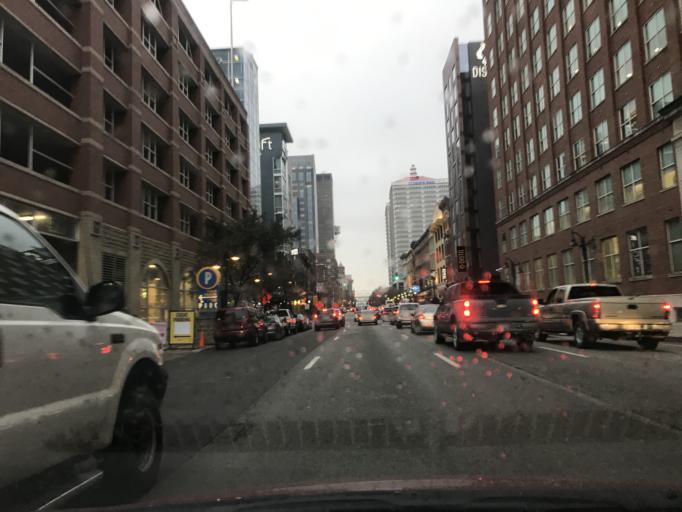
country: US
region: Kentucky
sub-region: Jefferson County
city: Louisville
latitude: 38.2560
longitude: -85.7508
